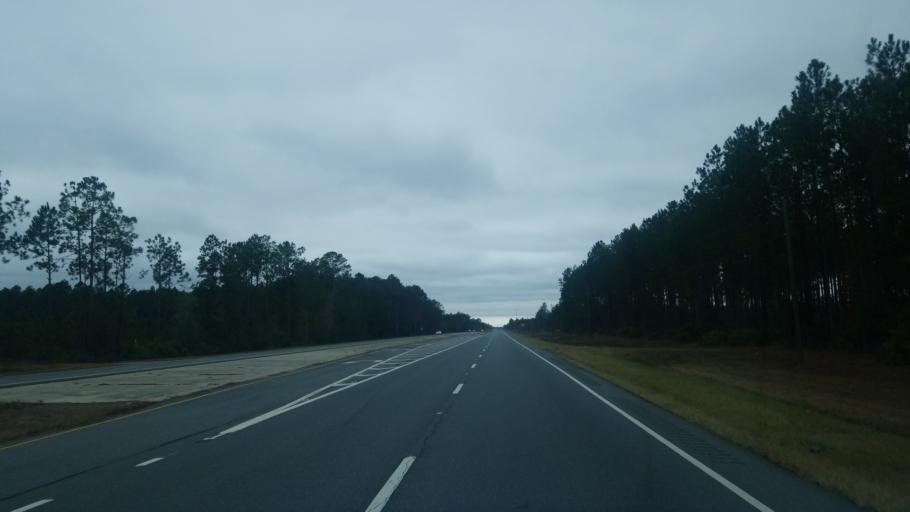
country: US
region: Georgia
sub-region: Charlton County
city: Folkston
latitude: 30.8841
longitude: -82.0397
